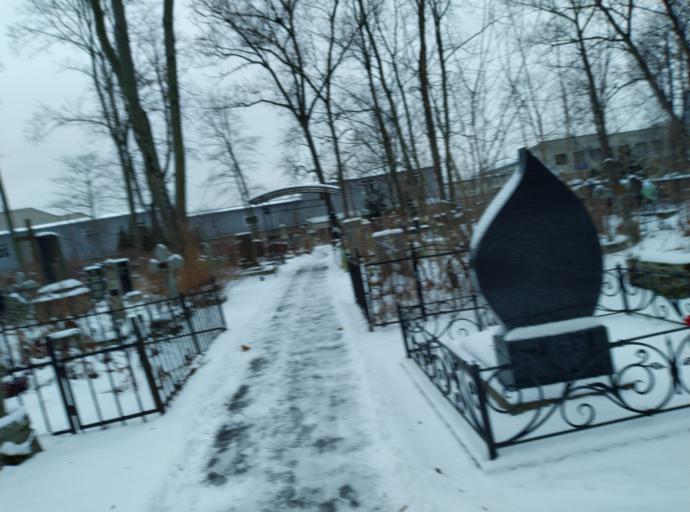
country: RU
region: St.-Petersburg
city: Centralniy
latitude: 59.9031
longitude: 30.3576
